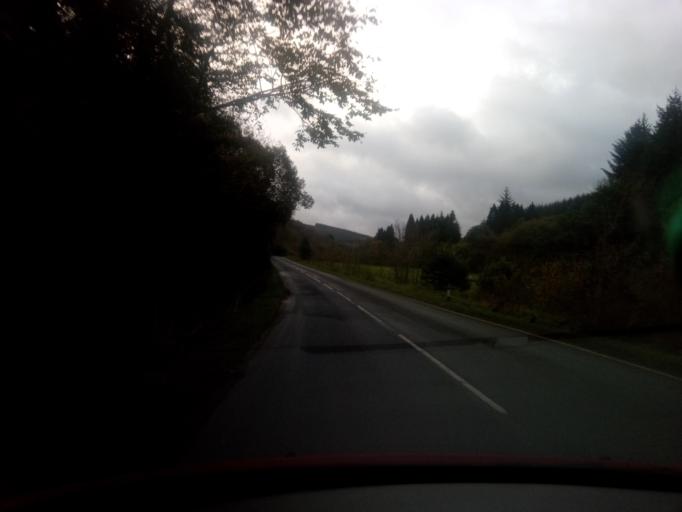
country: GB
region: Scotland
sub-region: The Scottish Borders
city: Hawick
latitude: 55.3600
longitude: -2.6499
